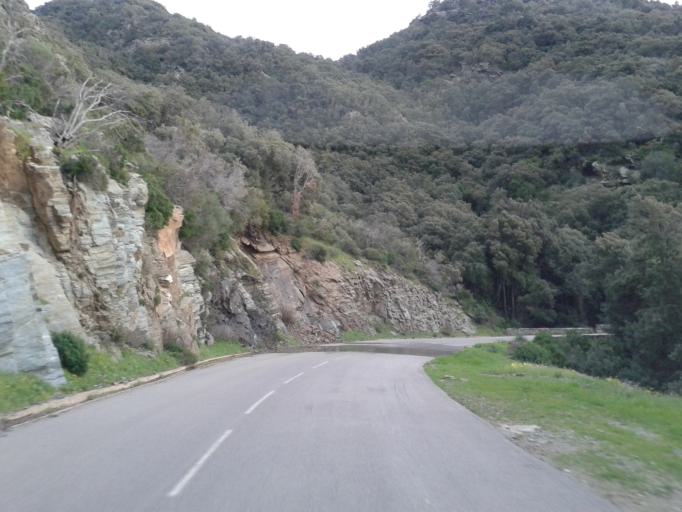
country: FR
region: Corsica
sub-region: Departement de la Haute-Corse
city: Brando
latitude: 42.8839
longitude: 9.3345
